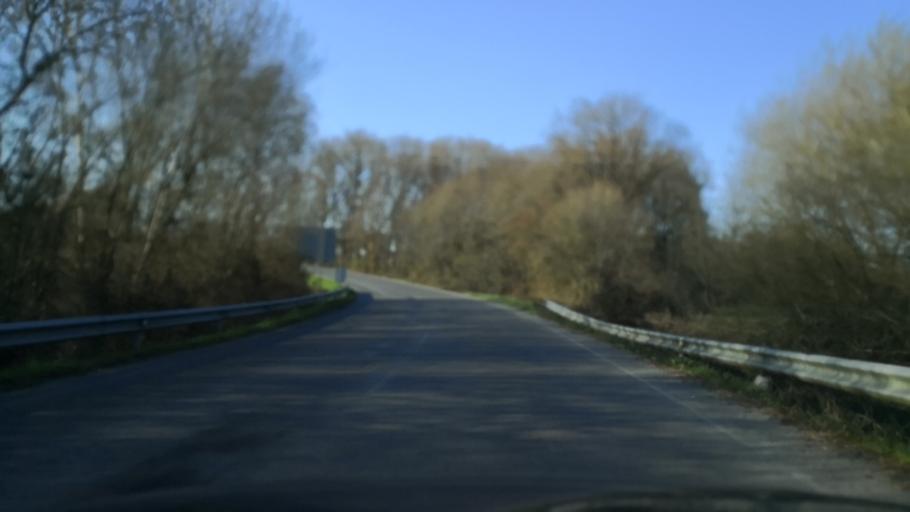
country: ES
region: Galicia
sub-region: Provincia de Lugo
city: Corgo
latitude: 42.9337
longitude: -7.3981
